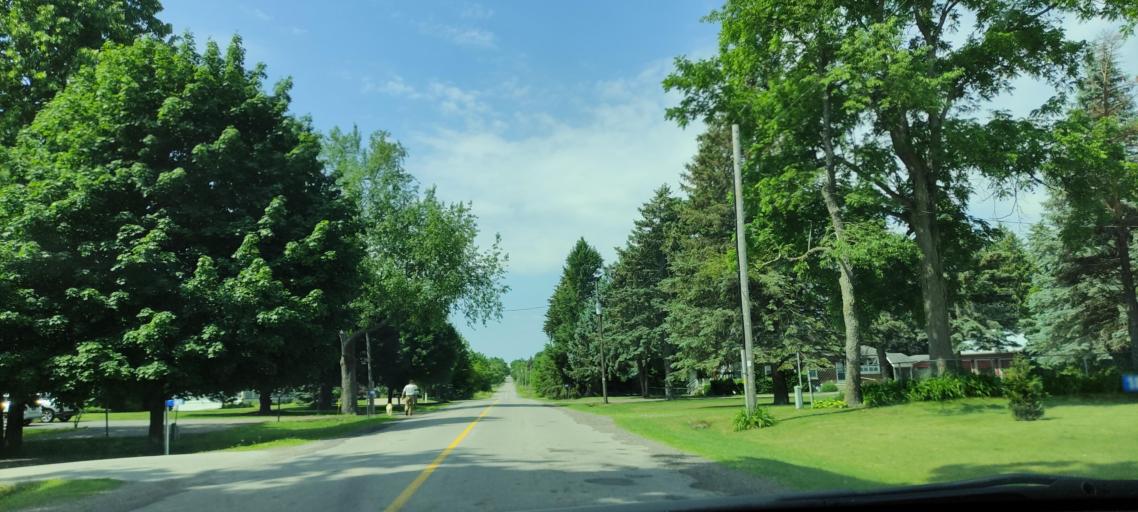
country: CA
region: Ontario
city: Burlington
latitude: 43.3655
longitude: -79.9583
